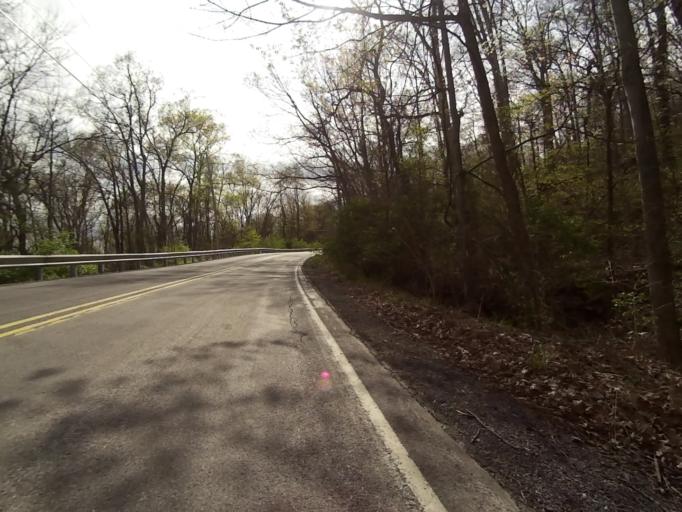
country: US
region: Pennsylvania
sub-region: Centre County
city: Stormstown
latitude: 40.8843
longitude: -77.9905
